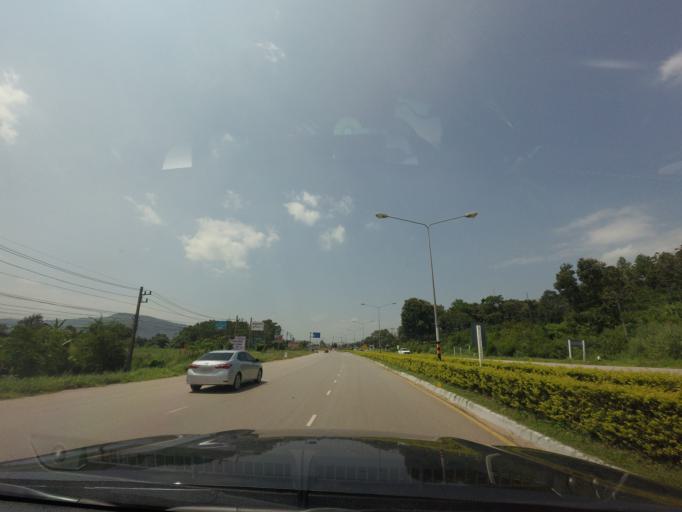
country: TH
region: Loei
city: Phu Ruea
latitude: 17.4559
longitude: 101.3661
